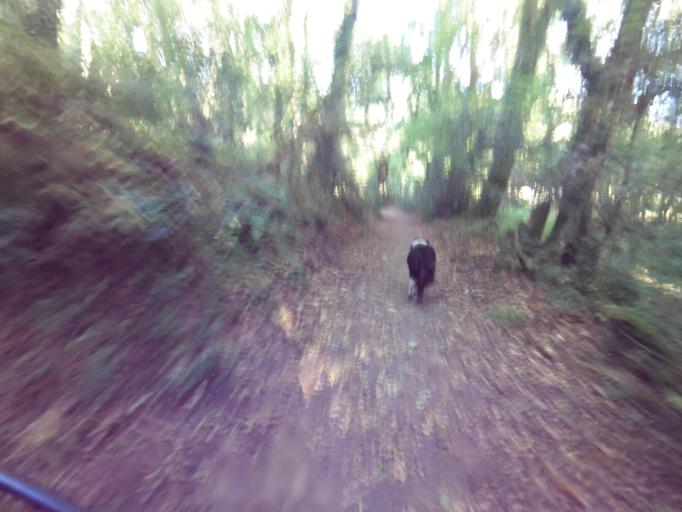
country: FR
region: Brittany
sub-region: Departement du Morbihan
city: Pluherlin
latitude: 47.7033
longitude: -2.3467
